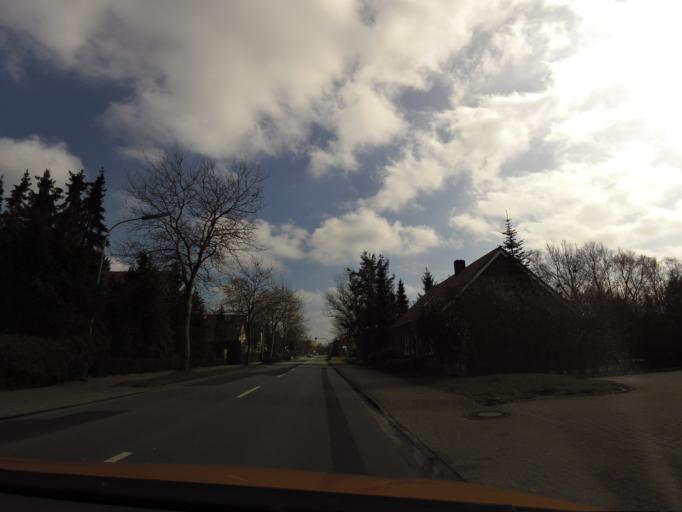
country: DE
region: Lower Saxony
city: Varel
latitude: 53.3854
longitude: 8.2347
